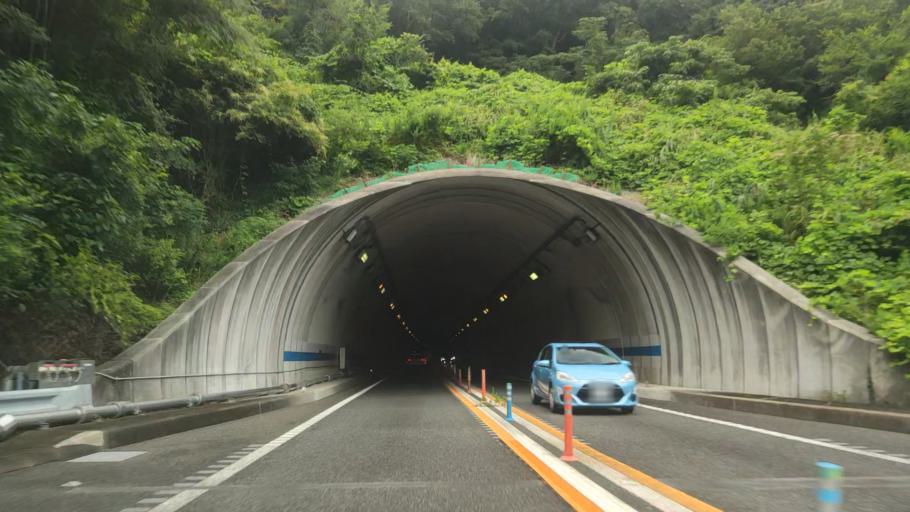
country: JP
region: Wakayama
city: Tanabe
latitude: 33.7918
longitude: 135.2916
